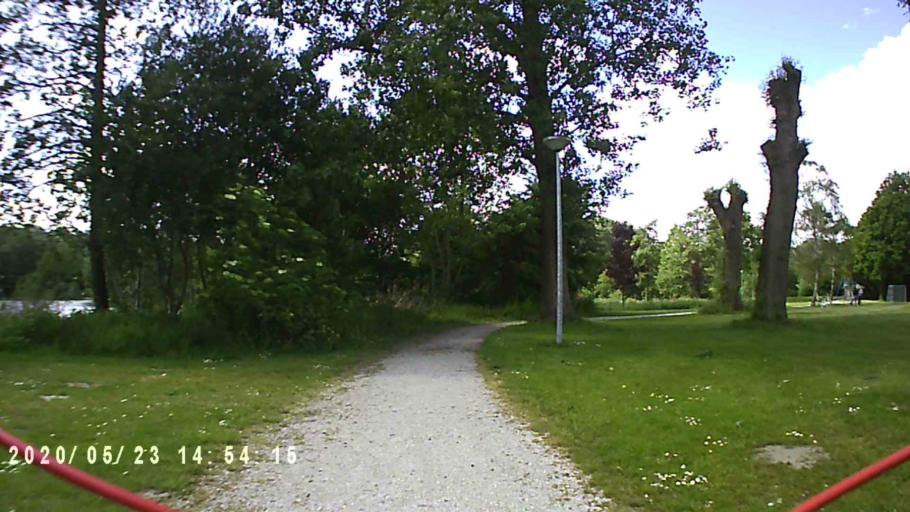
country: NL
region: Groningen
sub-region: Gemeente Delfzijl
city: Delfzijl
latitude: 53.2577
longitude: 6.9266
